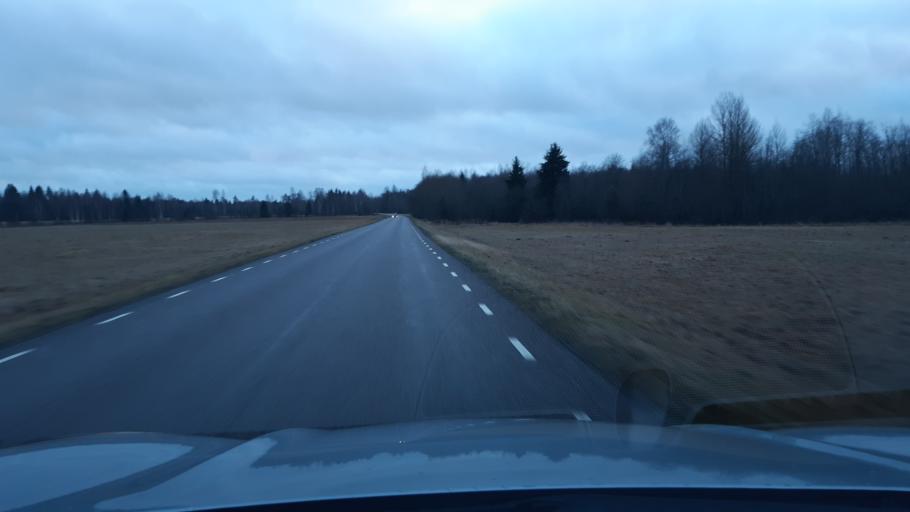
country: EE
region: Raplamaa
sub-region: Kohila vald
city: Kohila
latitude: 59.0906
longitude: 24.6740
